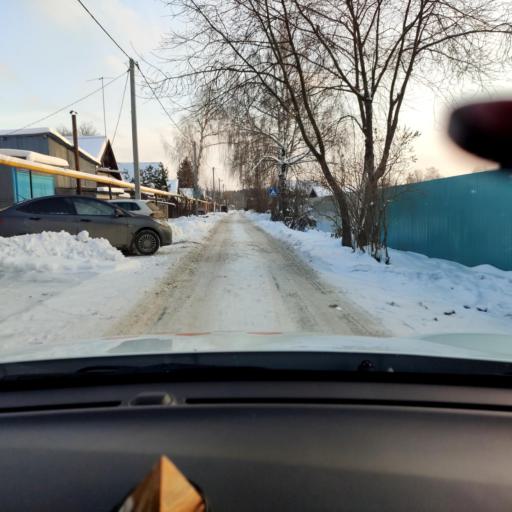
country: RU
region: Tatarstan
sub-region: Zelenodol'skiy Rayon
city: Vasil'yevo
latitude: 55.9083
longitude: 48.7474
